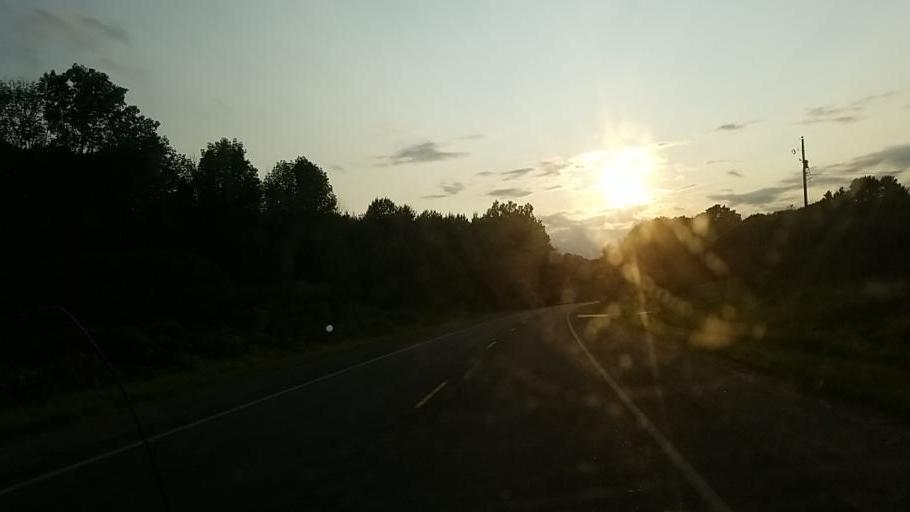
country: US
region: Michigan
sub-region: Newaygo County
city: Newaygo
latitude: 43.3976
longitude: -85.6489
